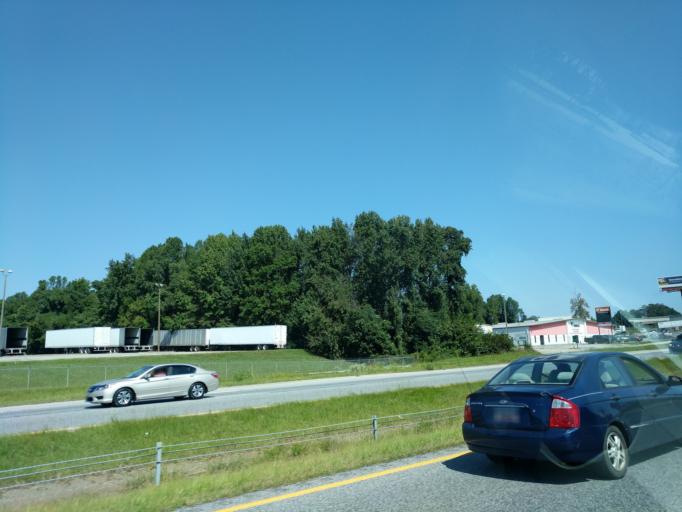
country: US
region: South Carolina
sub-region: Spartanburg County
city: Southern Shops
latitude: 34.9778
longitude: -81.9807
